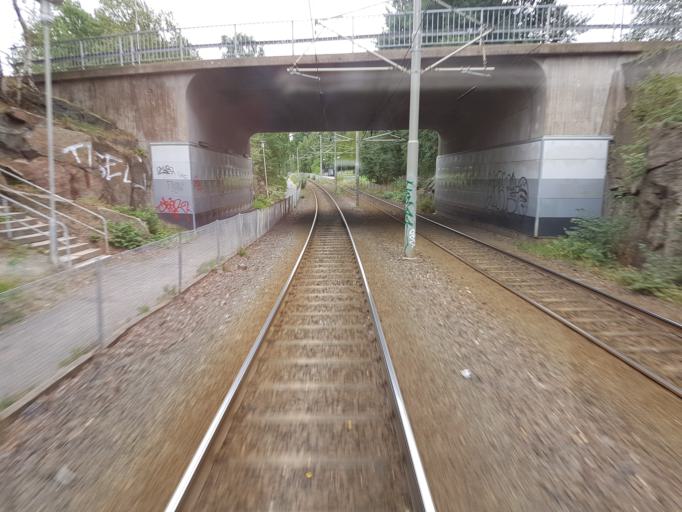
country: SE
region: Vaestra Goetaland
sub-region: Goteborg
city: Majorna
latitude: 57.6681
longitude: 11.9246
